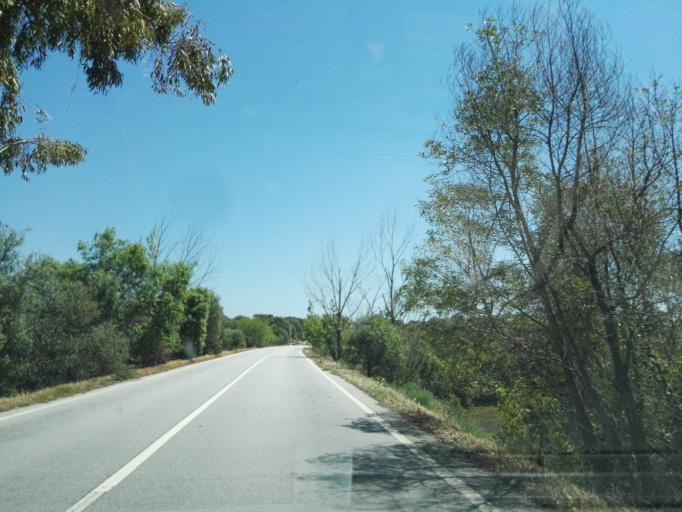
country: PT
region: Portalegre
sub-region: Elvas
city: Elvas
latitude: 39.0014
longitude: -7.2155
